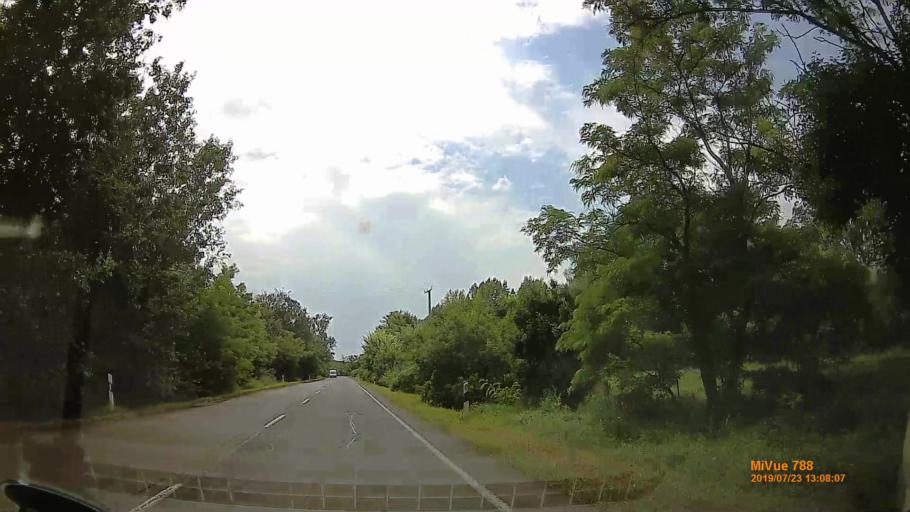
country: HU
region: Szabolcs-Szatmar-Bereg
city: Tiszavasvari
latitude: 47.9487
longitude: 21.3272
